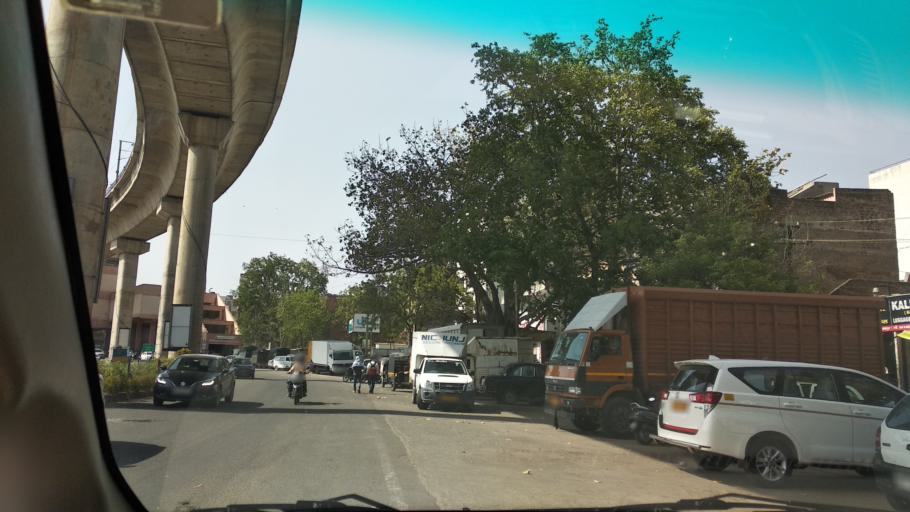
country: IN
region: Rajasthan
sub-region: Jaipur
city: Jaipur
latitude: 26.9161
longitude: 75.7910
